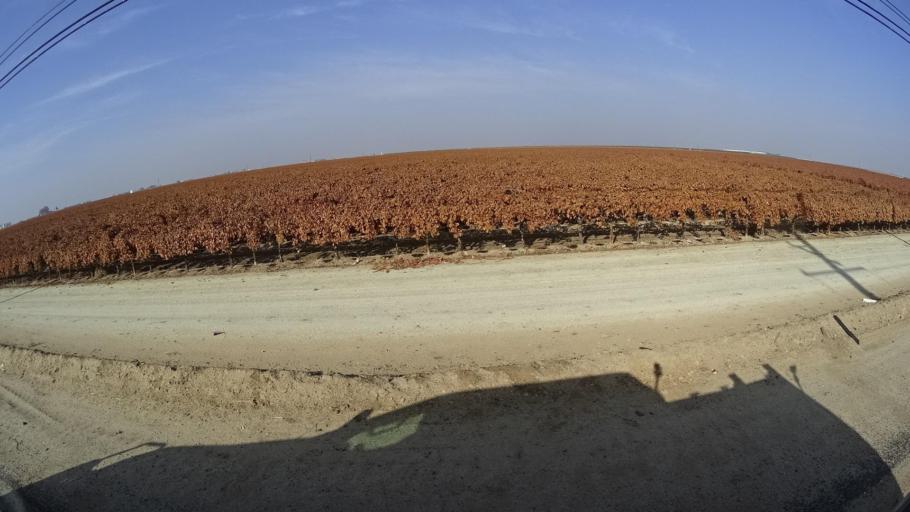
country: US
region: California
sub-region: Tulare County
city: Richgrove
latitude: 35.7760
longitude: -119.1747
